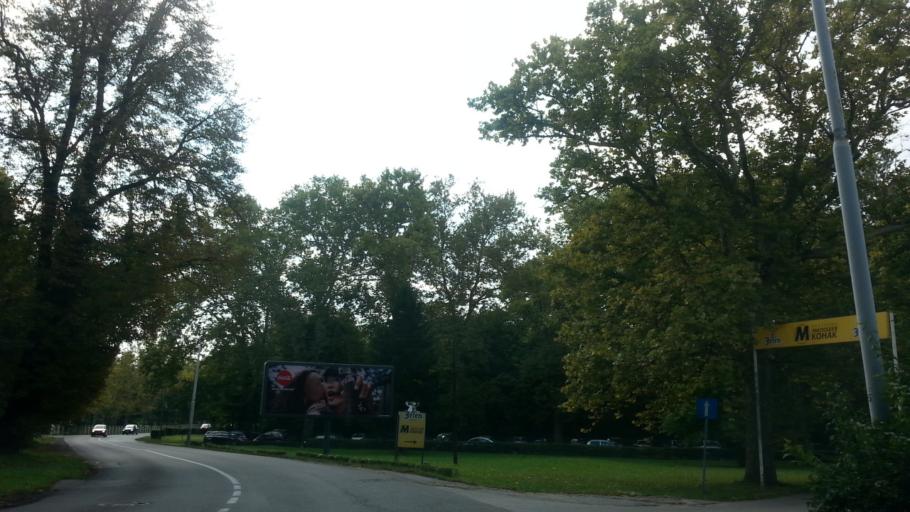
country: RS
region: Central Serbia
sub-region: Belgrade
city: Savski Venac
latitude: 44.7800
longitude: 20.4421
